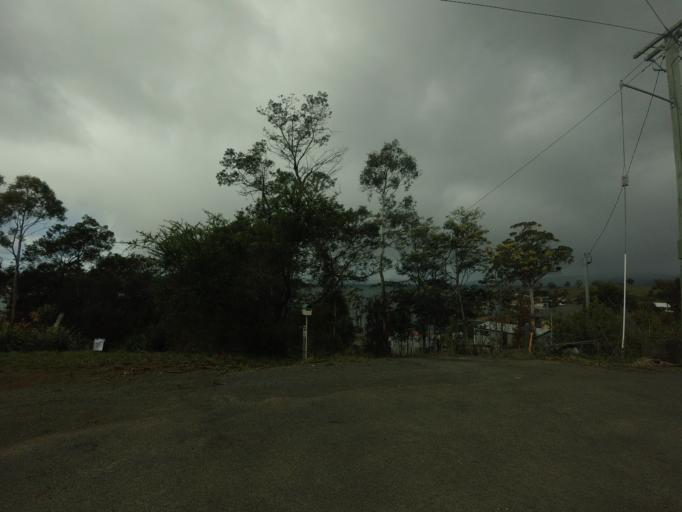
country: AU
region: Tasmania
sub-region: Sorell
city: Sorell
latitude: -42.5378
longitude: 147.9137
